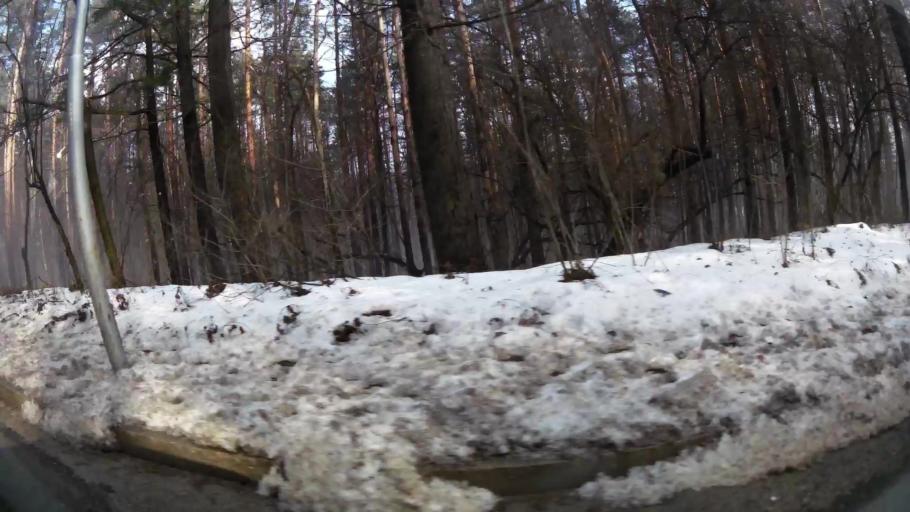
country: BG
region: Sofia-Capital
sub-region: Stolichna Obshtina
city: Sofia
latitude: 42.6495
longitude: 23.2434
